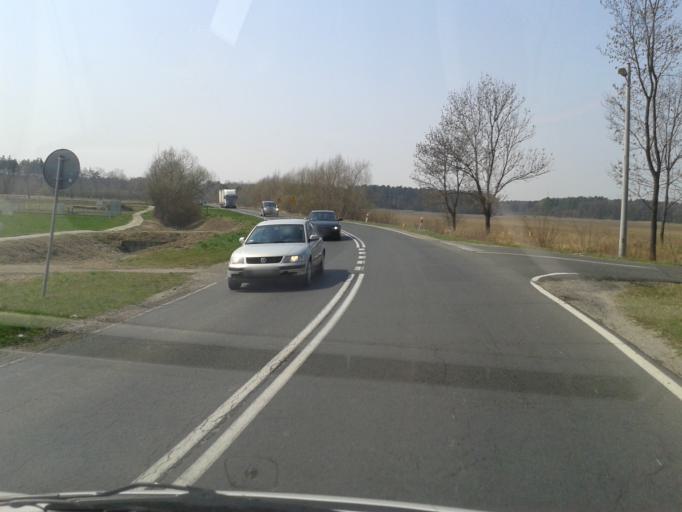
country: PL
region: Subcarpathian Voivodeship
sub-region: Powiat jaroslawski
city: Laszki
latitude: 50.0769
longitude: 22.8411
